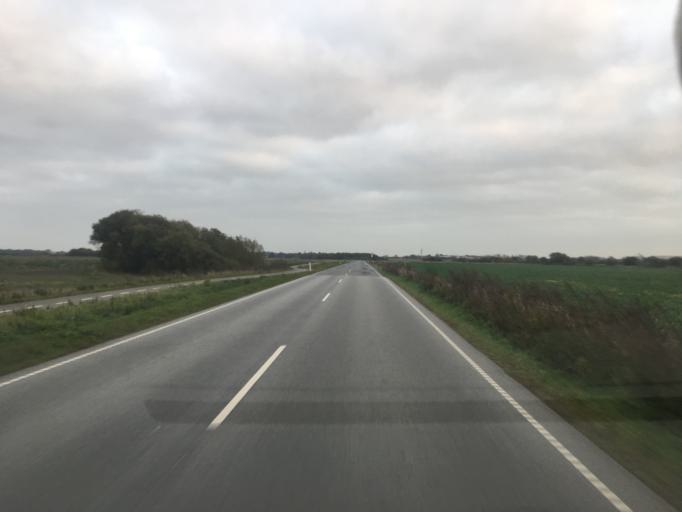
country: DE
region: Schleswig-Holstein
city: Aventoft
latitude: 54.9590
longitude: 8.7635
